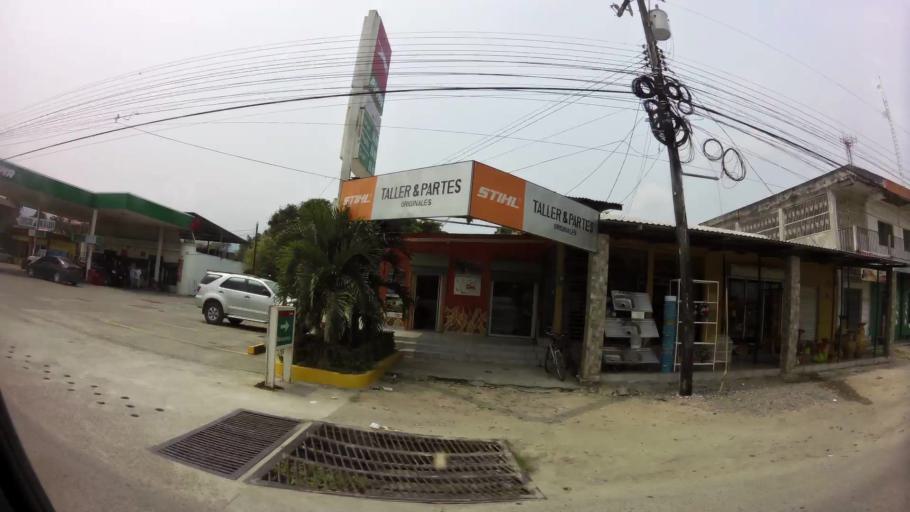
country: HN
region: Atlantida
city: San Juan Pueblo
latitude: 15.5986
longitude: -87.2128
